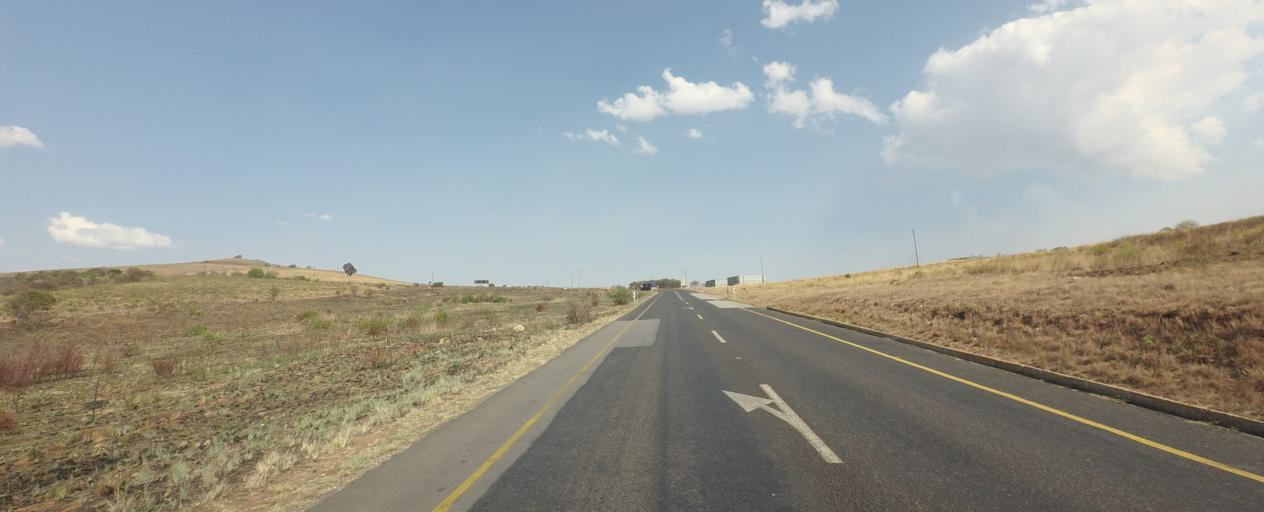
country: ZA
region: Mpumalanga
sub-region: Ehlanzeni District
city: Lydenburg
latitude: -25.1084
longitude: 30.4941
